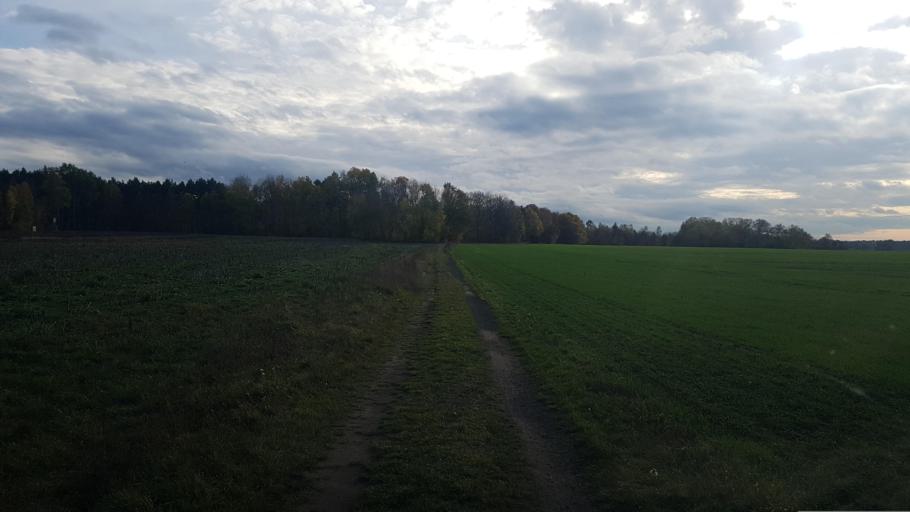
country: DE
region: Brandenburg
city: Wiesenburg
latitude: 52.0792
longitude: 12.4635
